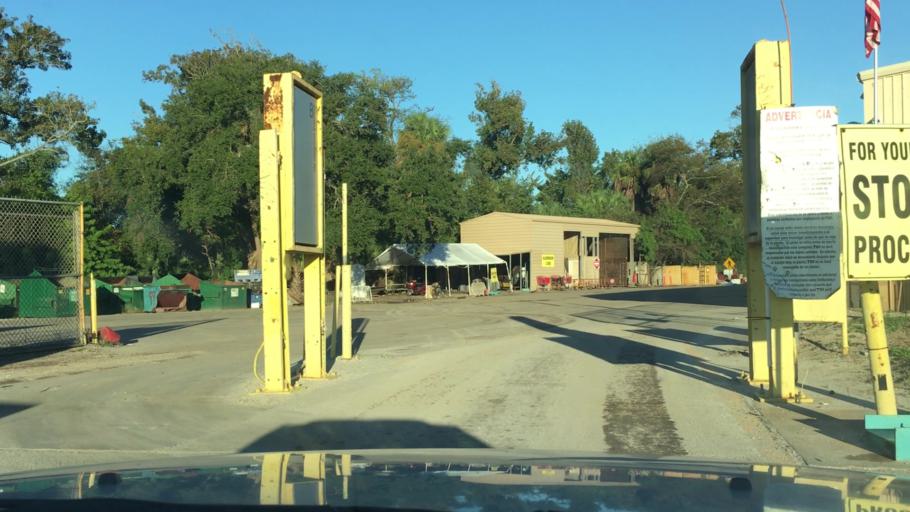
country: US
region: Florida
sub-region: Volusia County
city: Holly Hill
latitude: 29.2313
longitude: -81.0372
